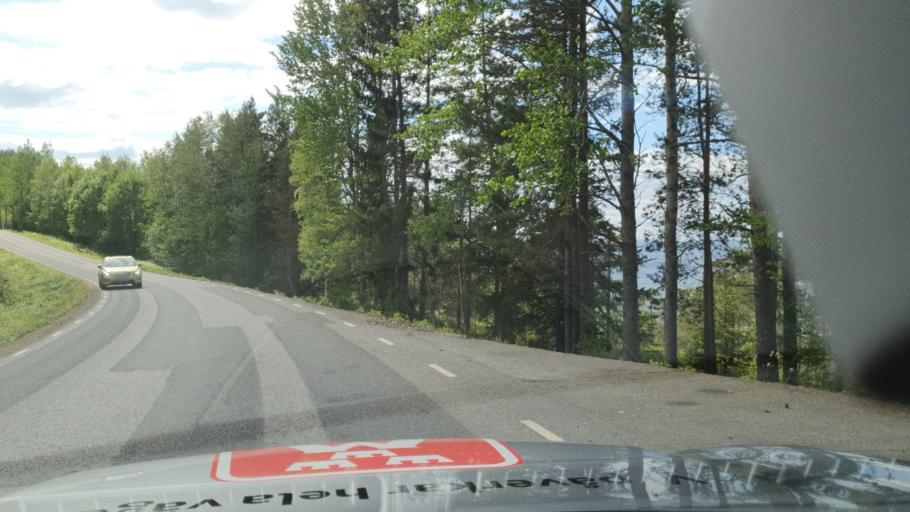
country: SE
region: Vaesternorrland
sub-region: Kramfors Kommun
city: Nordingra
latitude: 62.8113
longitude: 18.1389
